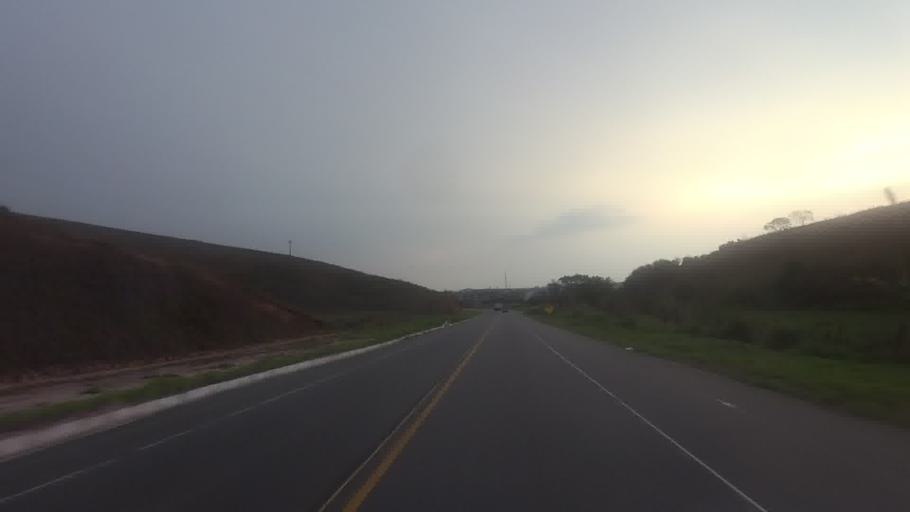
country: BR
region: Rio de Janeiro
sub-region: Carmo
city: Carmo
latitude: -21.7633
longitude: -42.5271
